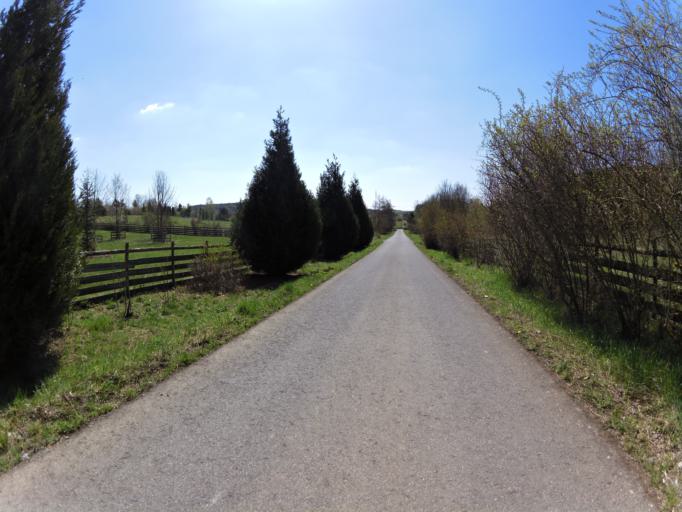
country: DE
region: Bavaria
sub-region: Regierungsbezirk Unterfranken
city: Greussenheim
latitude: 49.8172
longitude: 9.7928
